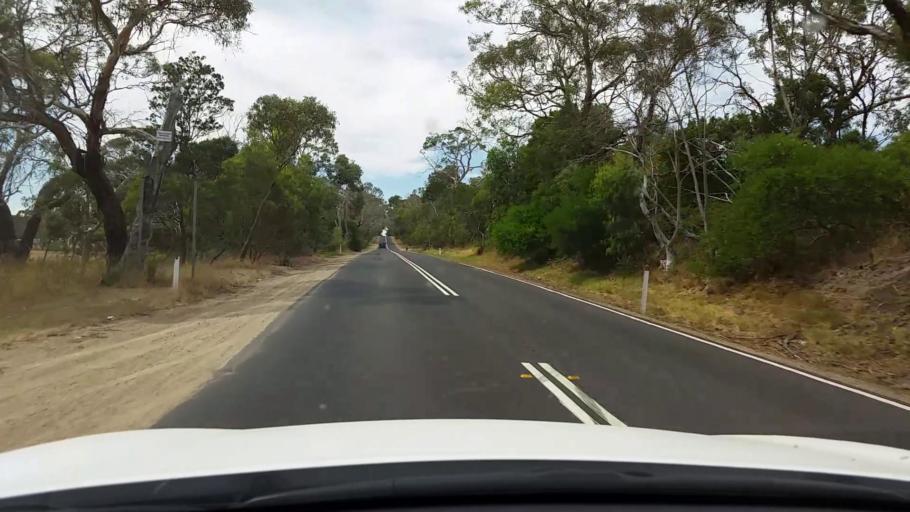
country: AU
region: Victoria
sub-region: Mornington Peninsula
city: Mount Martha
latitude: -38.2955
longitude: 145.0469
